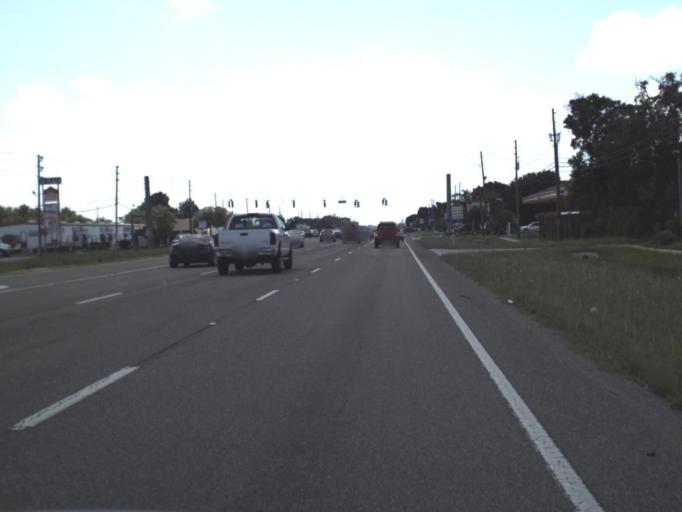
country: US
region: Florida
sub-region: Pinellas County
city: South Highpoint
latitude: 27.8879
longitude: -82.7293
